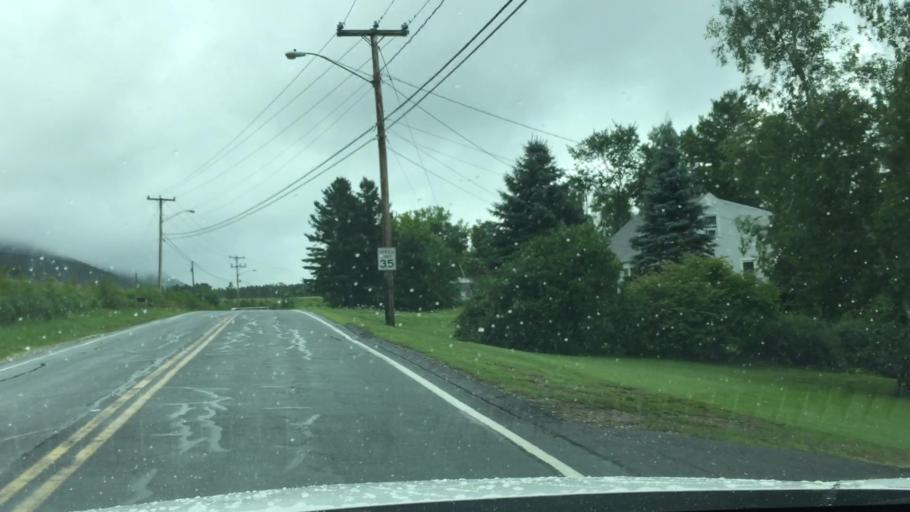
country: US
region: Massachusetts
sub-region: Berkshire County
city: Pittsfield
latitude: 42.4279
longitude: -73.2990
